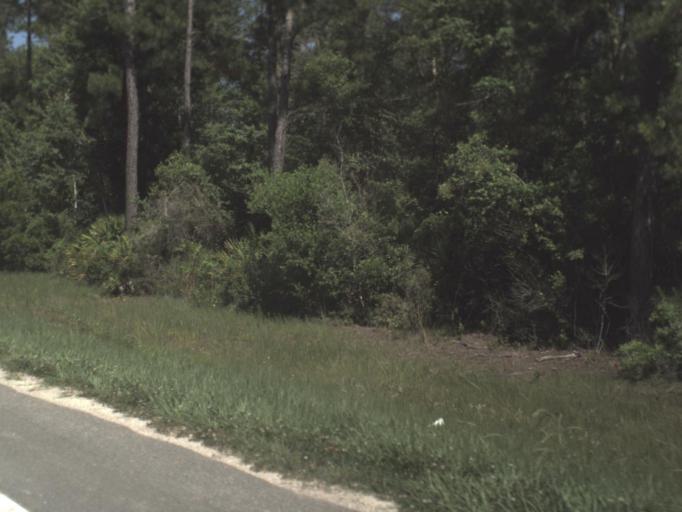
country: US
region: Florida
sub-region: Baker County
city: Macclenny
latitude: 30.2856
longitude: -82.1032
